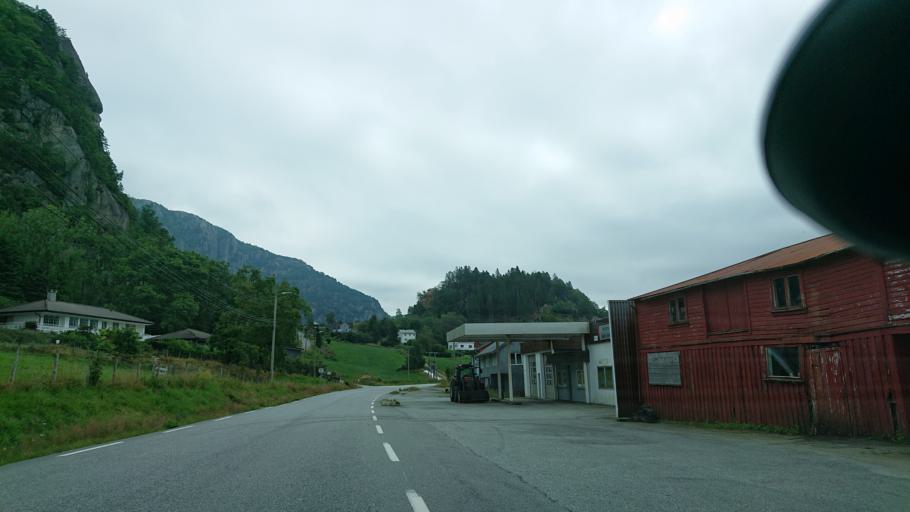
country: NO
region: Rogaland
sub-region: Hjelmeland
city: Hjelmelandsvagen
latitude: 59.2345
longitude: 6.1861
